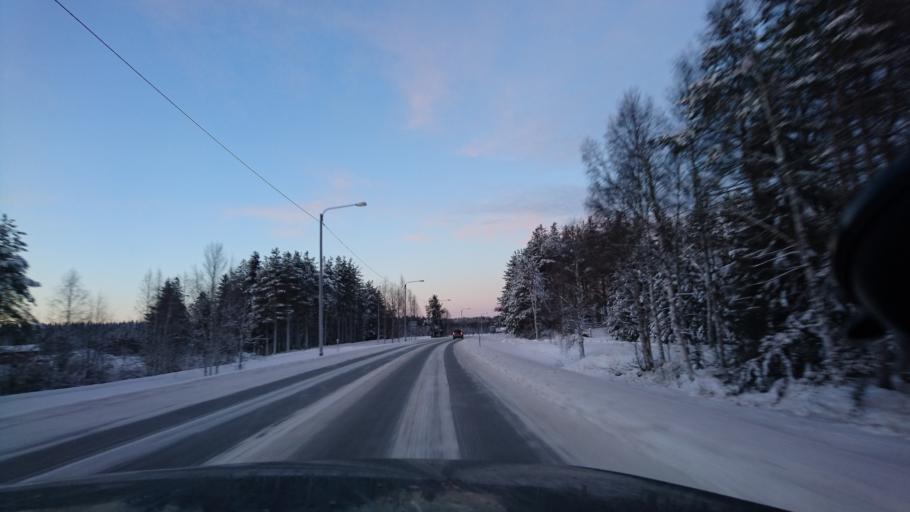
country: FI
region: Lapland
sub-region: Rovaniemi
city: Ranua
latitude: 65.9342
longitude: 26.4963
